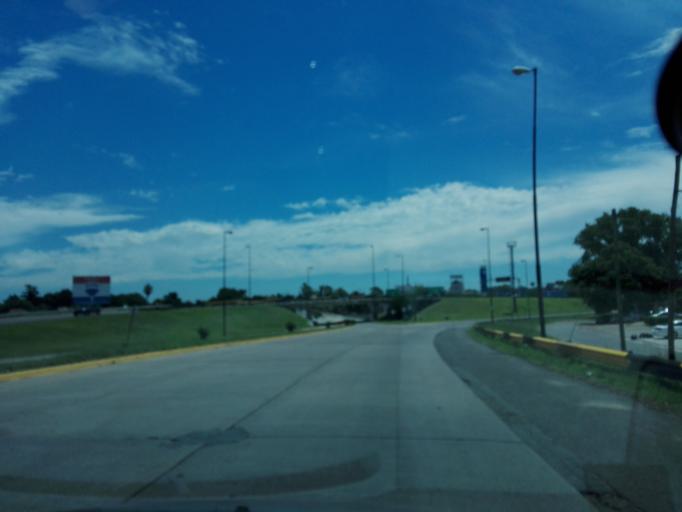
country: AR
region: Buenos Aires
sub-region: Partido de La Plata
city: La Plata
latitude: -34.8965
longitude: -57.9910
